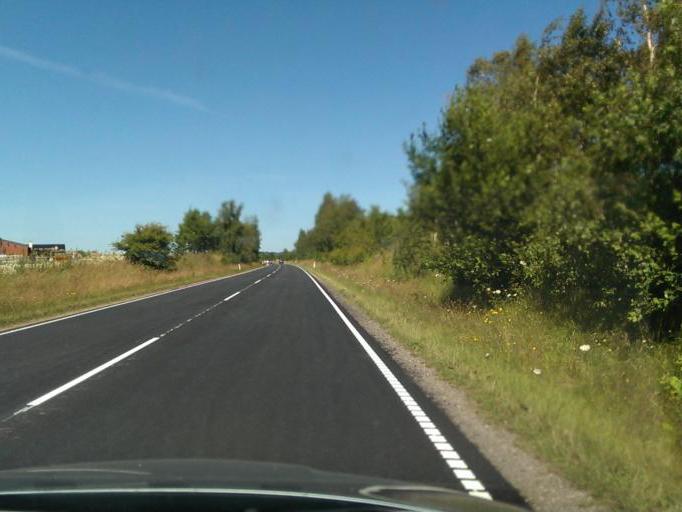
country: DK
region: Central Jutland
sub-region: Arhus Kommune
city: Malling
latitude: 56.0458
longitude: 10.1890
